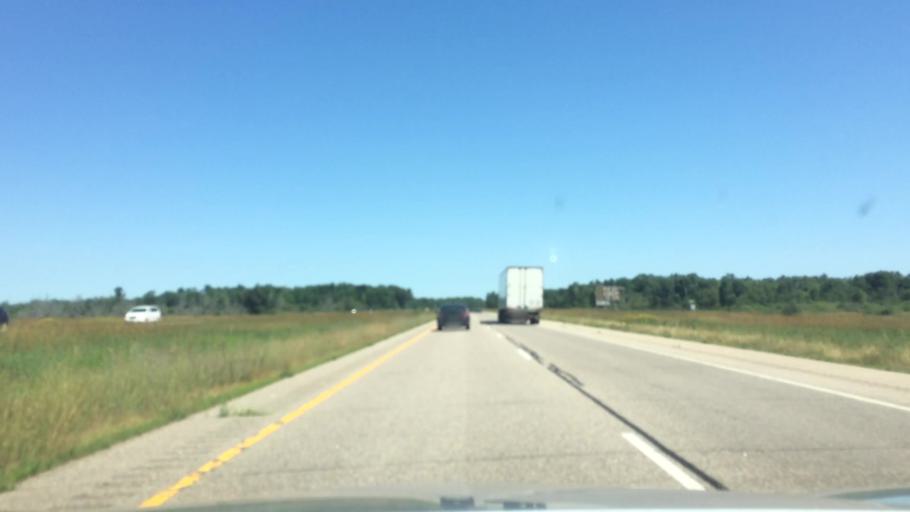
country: US
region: Wisconsin
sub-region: Waushara County
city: Wautoma
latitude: 44.1600
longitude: -89.5323
